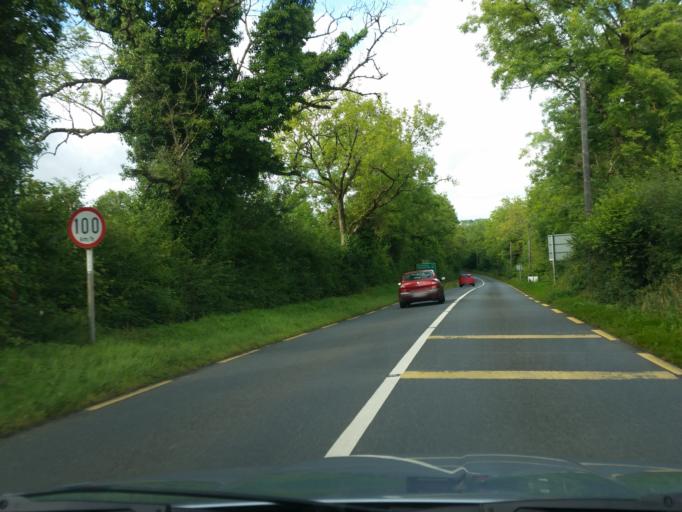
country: IE
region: Ulster
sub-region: An Cabhan
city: Belturbet
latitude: 54.1020
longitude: -7.3646
